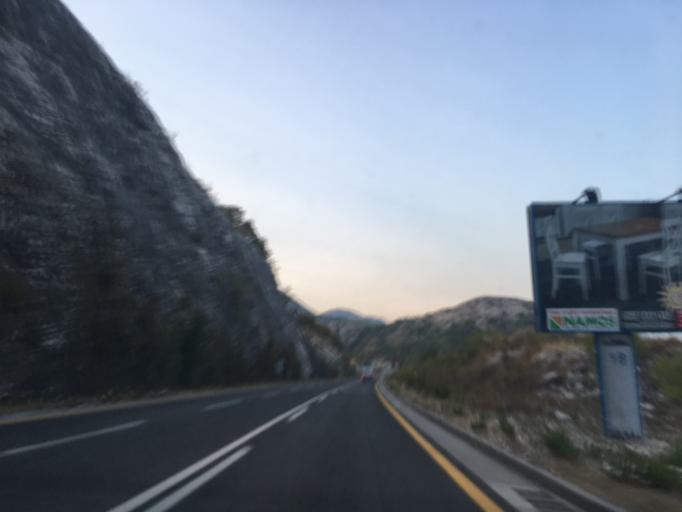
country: ME
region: Bar
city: Sutomore
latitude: 42.2141
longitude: 19.0486
